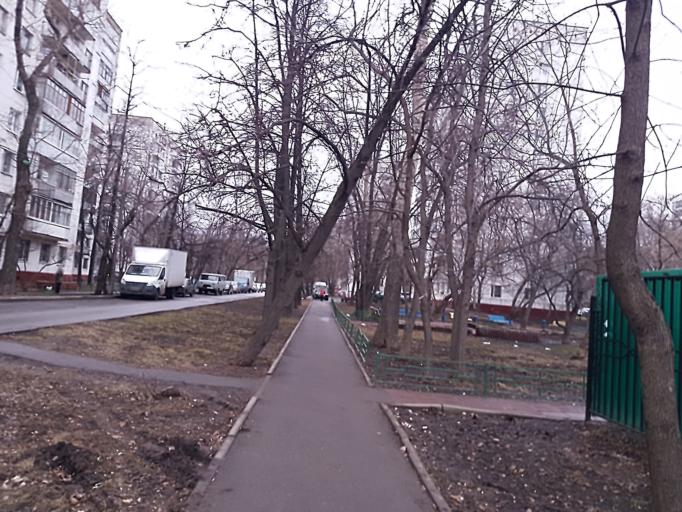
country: RU
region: Moskovskaya
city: Novogireyevo
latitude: 55.7535
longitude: 37.8131
